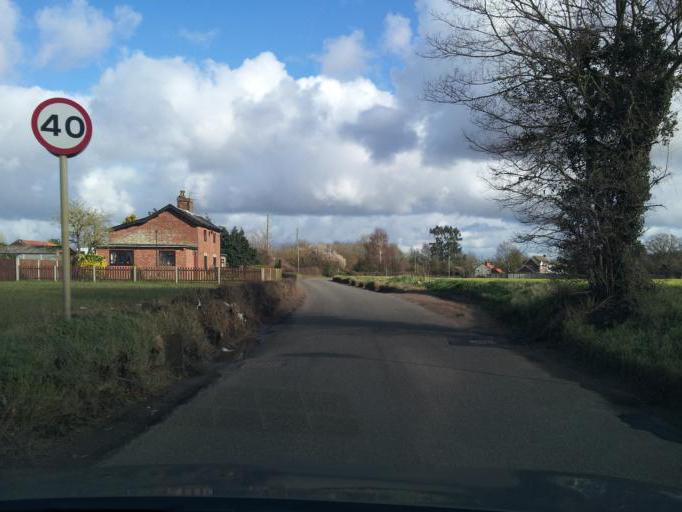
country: GB
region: England
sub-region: Norfolk
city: Mattishall
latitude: 52.6630
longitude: 1.0001
